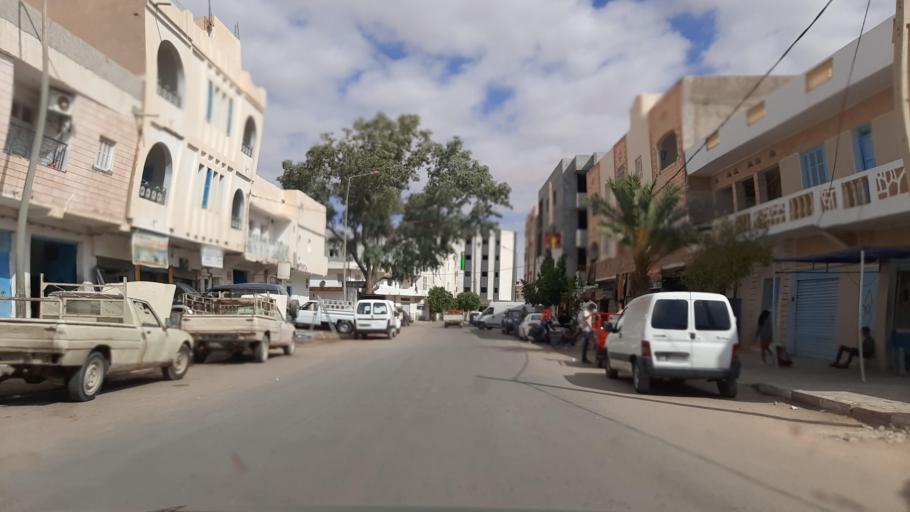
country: TN
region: Tataouine
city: Tataouine
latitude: 32.9322
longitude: 10.4532
